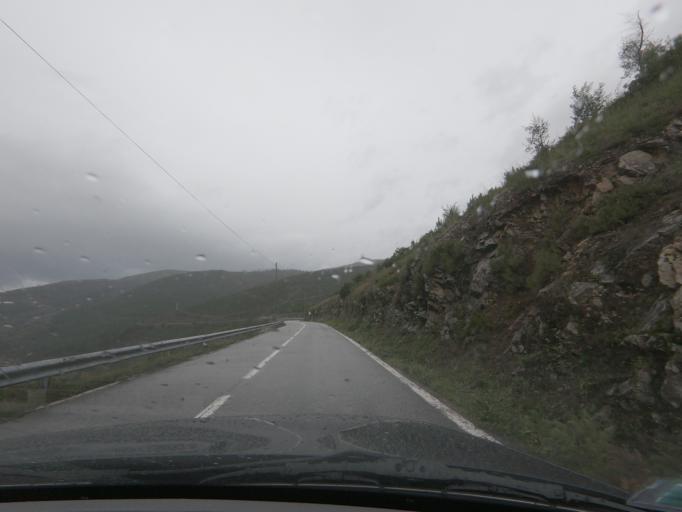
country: PT
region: Vila Real
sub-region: Mondim de Basto
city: Mondim de Basto
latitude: 41.3540
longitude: -7.9172
